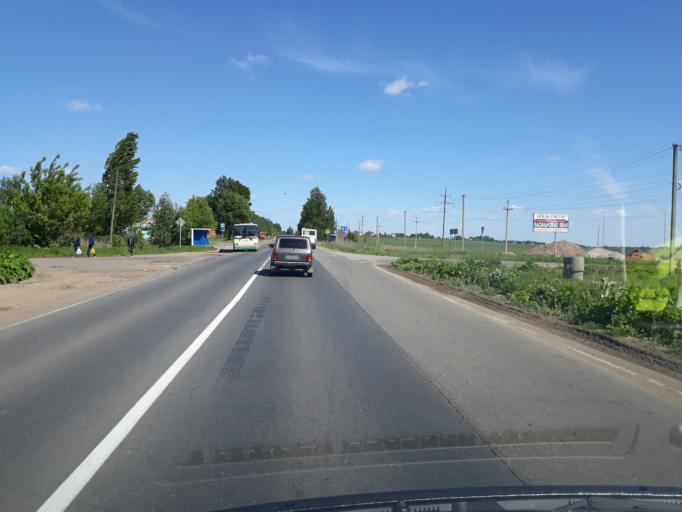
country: RU
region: Jaroslavl
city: Yaroslavl
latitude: 57.6686
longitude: 40.0111
